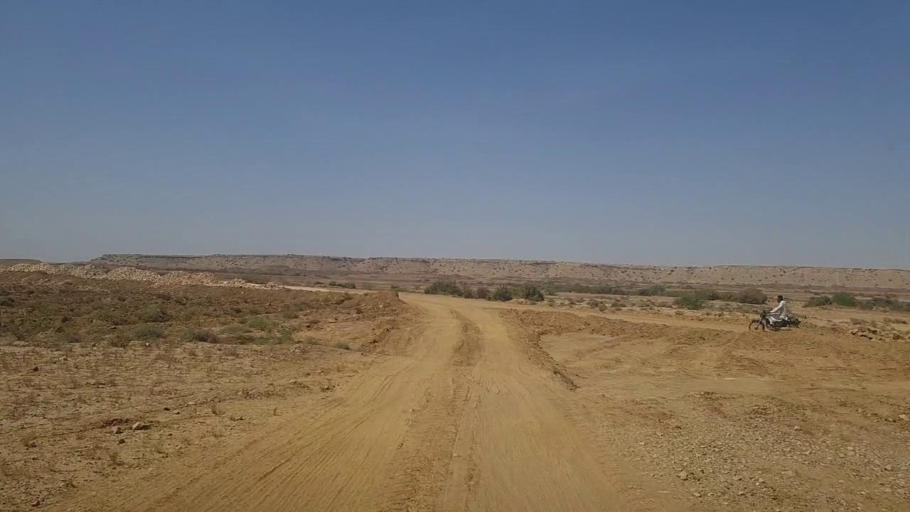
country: PK
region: Sindh
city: Kotri
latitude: 25.1467
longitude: 68.1772
